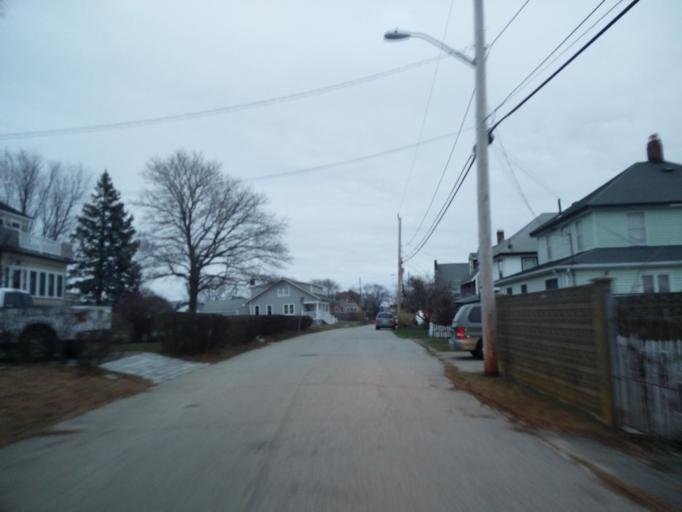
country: US
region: Massachusetts
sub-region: Plymouth County
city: Hingham
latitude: 42.2769
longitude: -70.8812
